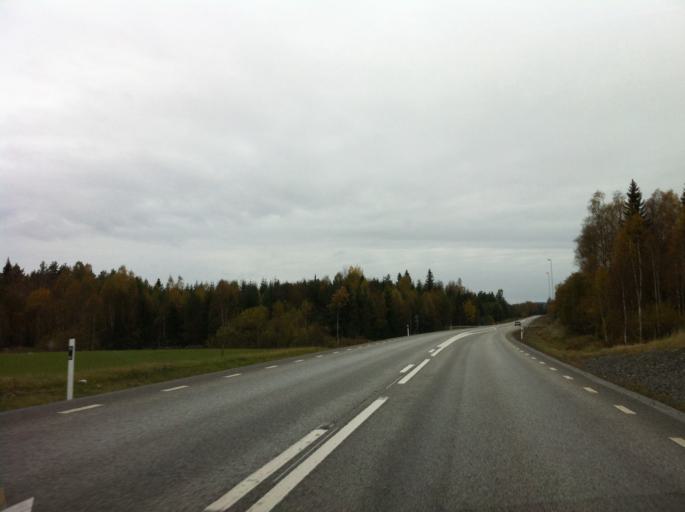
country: SE
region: OErebro
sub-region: Ljusnarsbergs Kommun
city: Kopparberg
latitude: 59.8460
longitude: 15.0717
